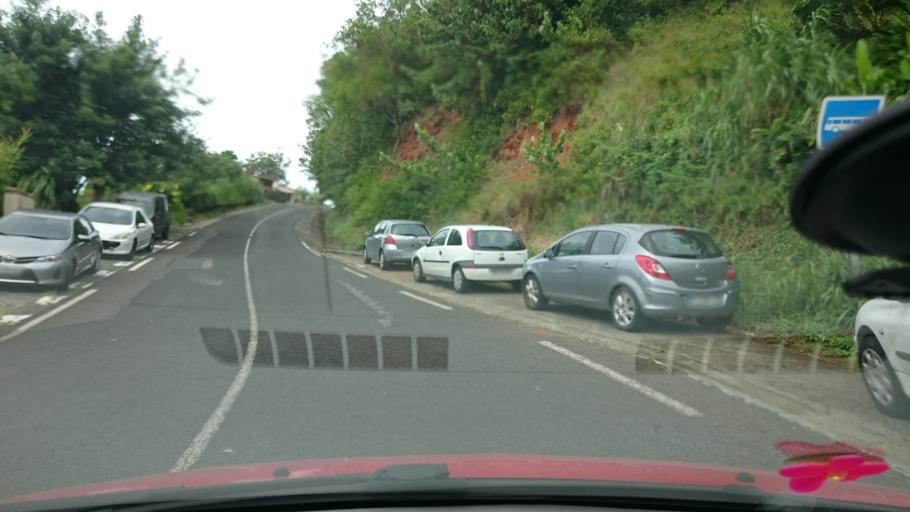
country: MQ
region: Martinique
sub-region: Martinique
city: Riviere-Pilote
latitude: 14.4959
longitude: -60.9239
